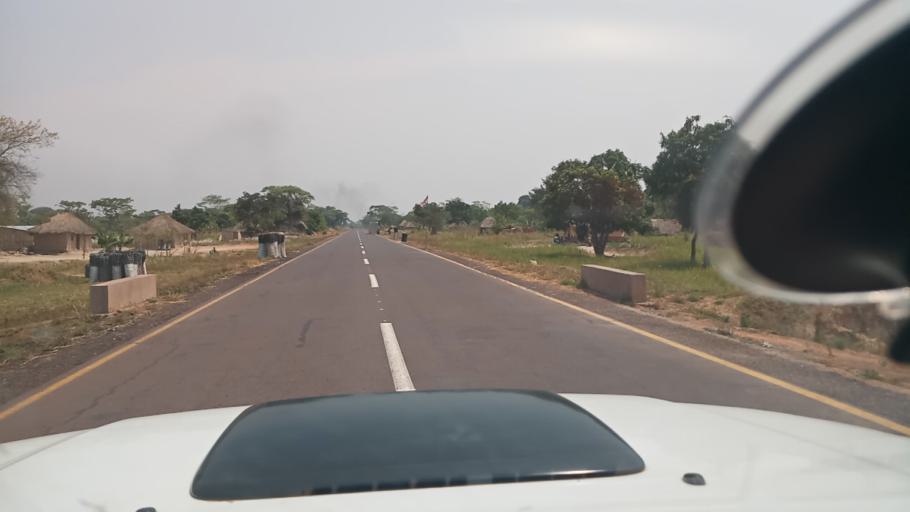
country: ZM
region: Luapula
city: Mwense
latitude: -10.8046
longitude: 28.2329
